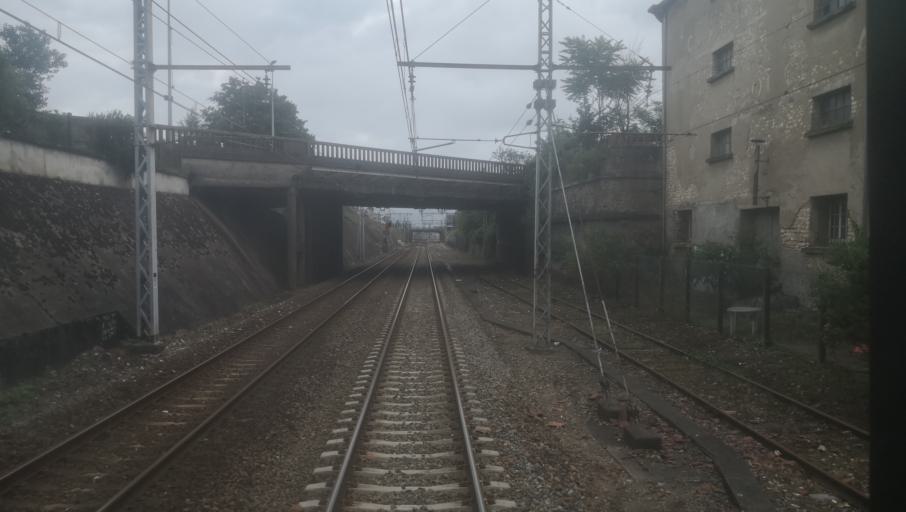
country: FR
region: Centre
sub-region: Departement de l'Indre
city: Chateauroux
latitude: 46.8047
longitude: 1.6883
